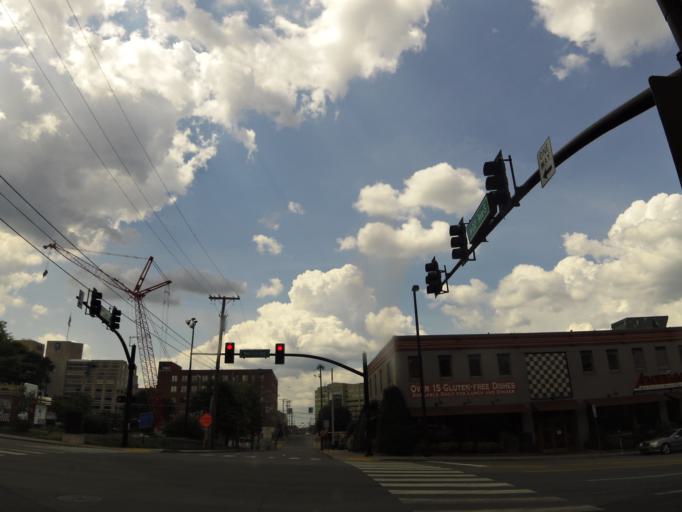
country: US
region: Tennessee
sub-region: Davidson County
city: Nashville
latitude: 36.1513
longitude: -86.7992
